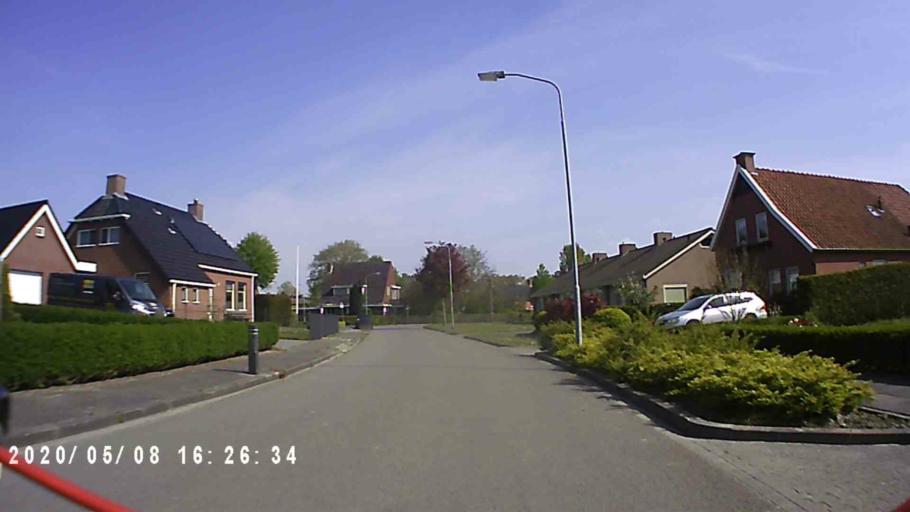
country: NL
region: Groningen
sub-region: Gemeente Bedum
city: Bedum
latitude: 53.3645
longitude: 6.6327
